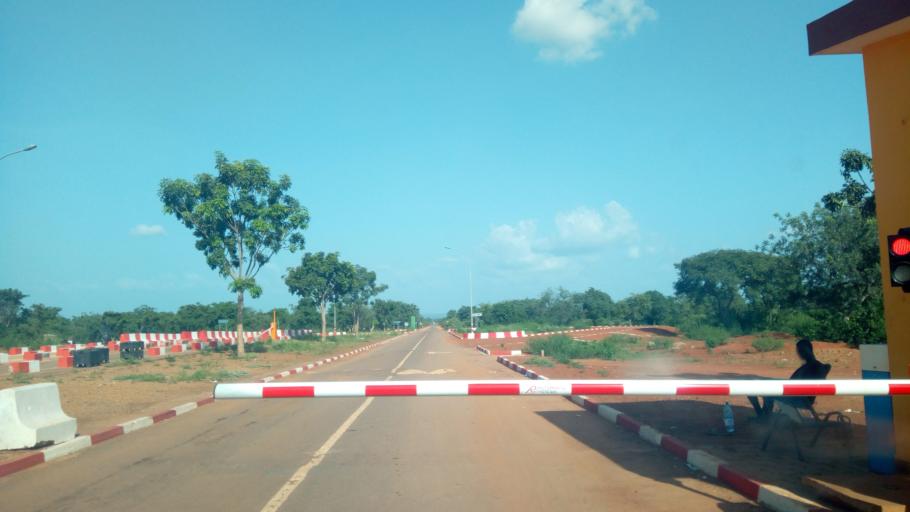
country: ML
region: Sikasso
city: Yorosso
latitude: 12.1851
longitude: -4.8310
